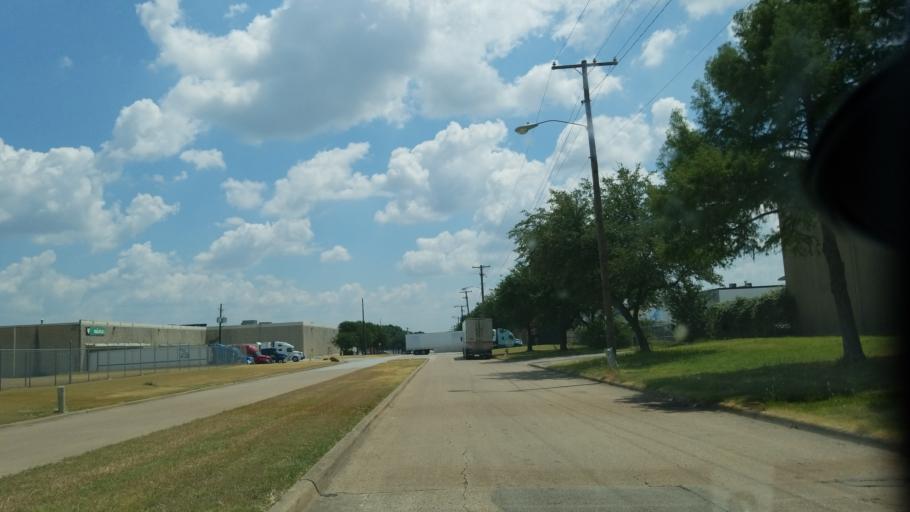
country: US
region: Texas
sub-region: Dallas County
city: Duncanville
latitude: 32.6872
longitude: -96.8972
